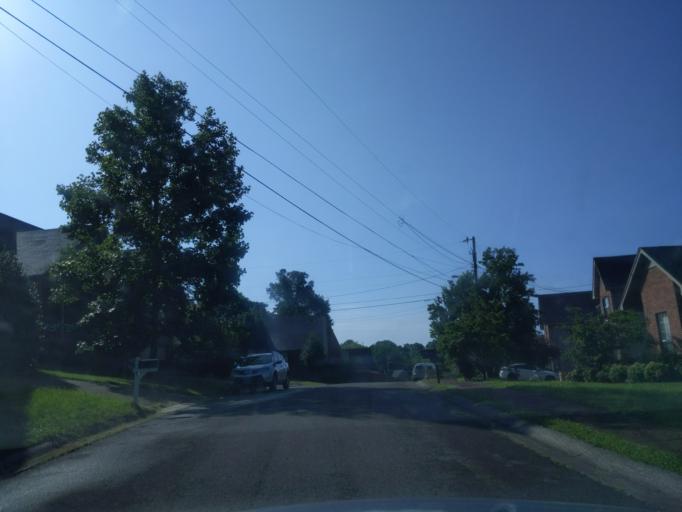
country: US
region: Tennessee
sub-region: Williamson County
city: Brentwood Estates
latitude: 36.0215
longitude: -86.7272
